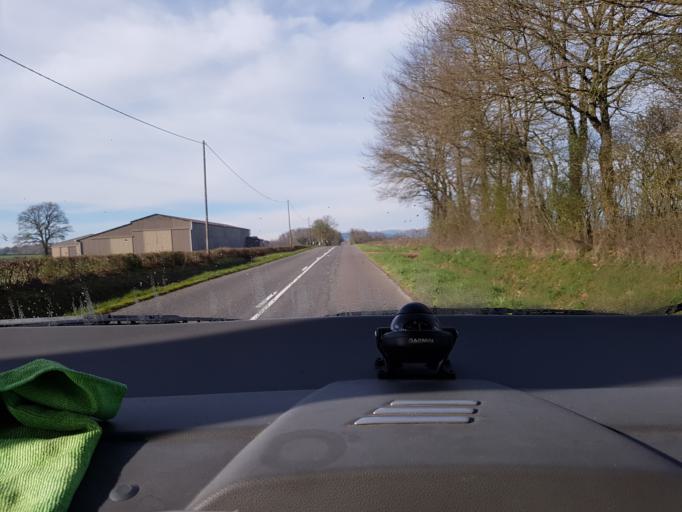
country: FR
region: Bourgogne
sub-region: Departement de Saone-et-Loire
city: Etang-sur-Arroux
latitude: 46.8255
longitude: 4.1757
